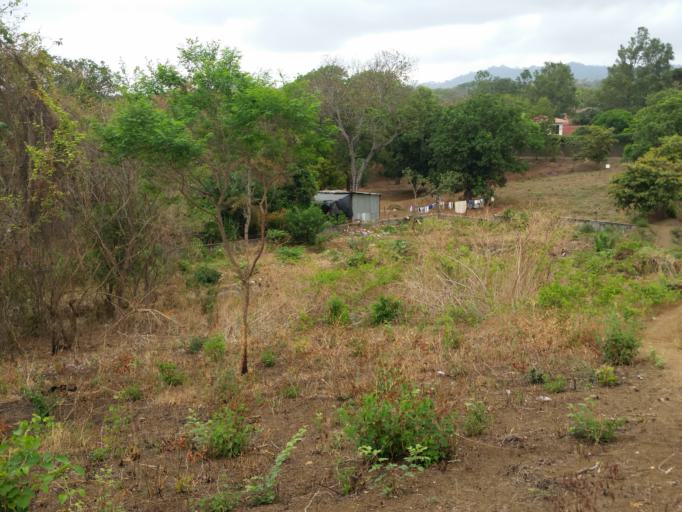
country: NI
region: Managua
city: Managua
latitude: 12.0779
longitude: -86.2529
